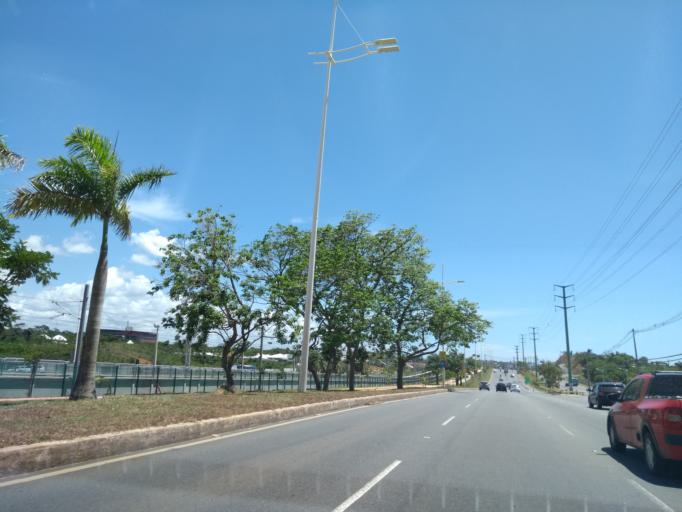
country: BR
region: Bahia
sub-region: Lauro De Freitas
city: Lauro de Freitas
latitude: -12.9312
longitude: -38.3899
